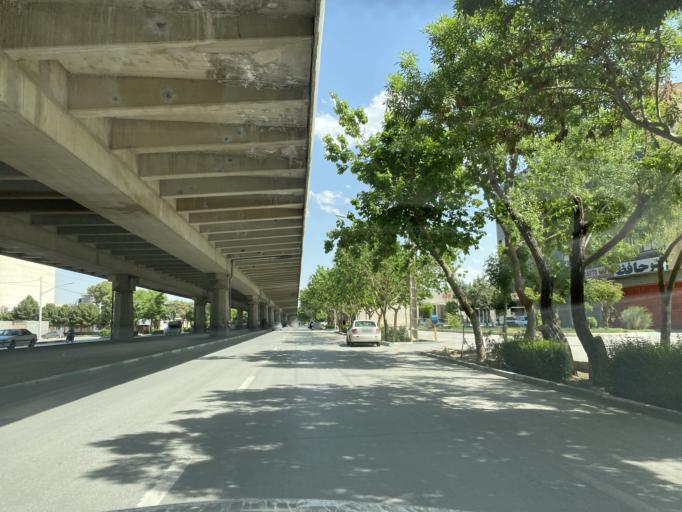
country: IR
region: Isfahan
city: Rehnan
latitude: 32.6914
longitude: 51.6284
